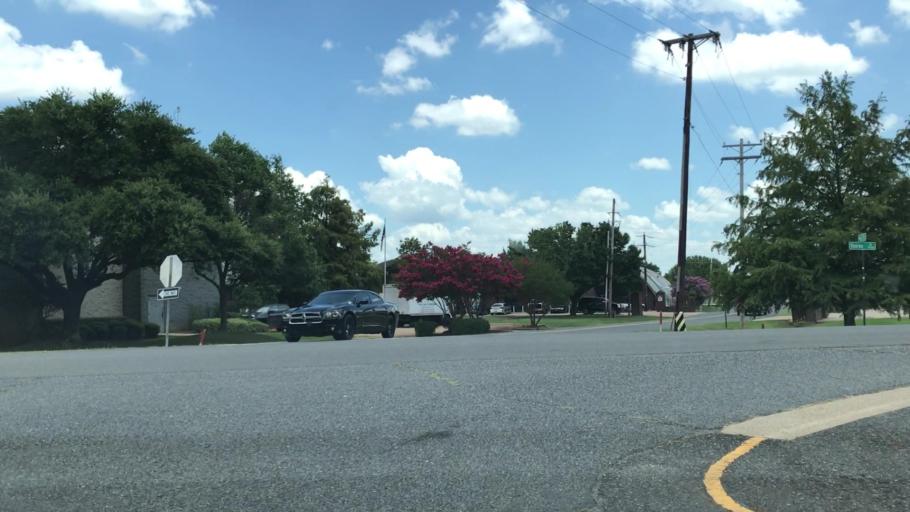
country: US
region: Louisiana
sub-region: Bossier Parish
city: Bossier City
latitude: 32.4081
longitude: -93.6982
